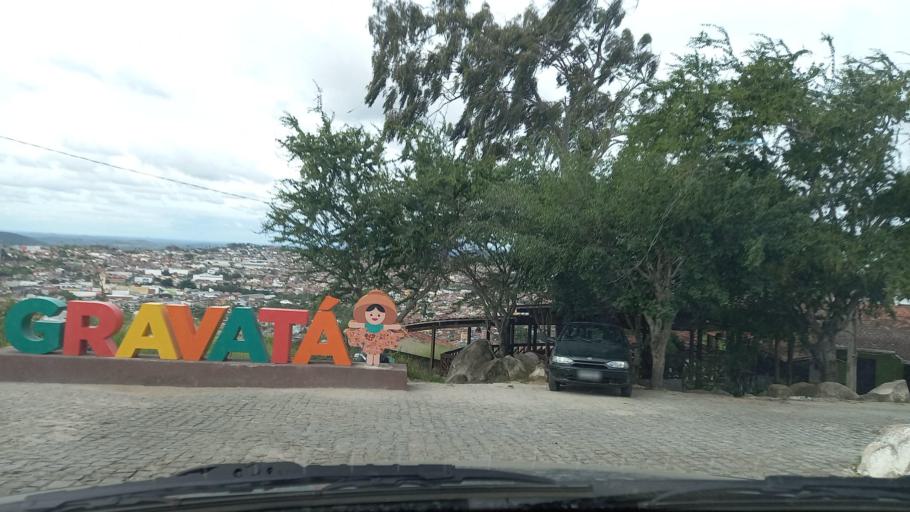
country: BR
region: Pernambuco
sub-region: Gravata
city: Gravata
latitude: -8.2107
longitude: -35.5742
